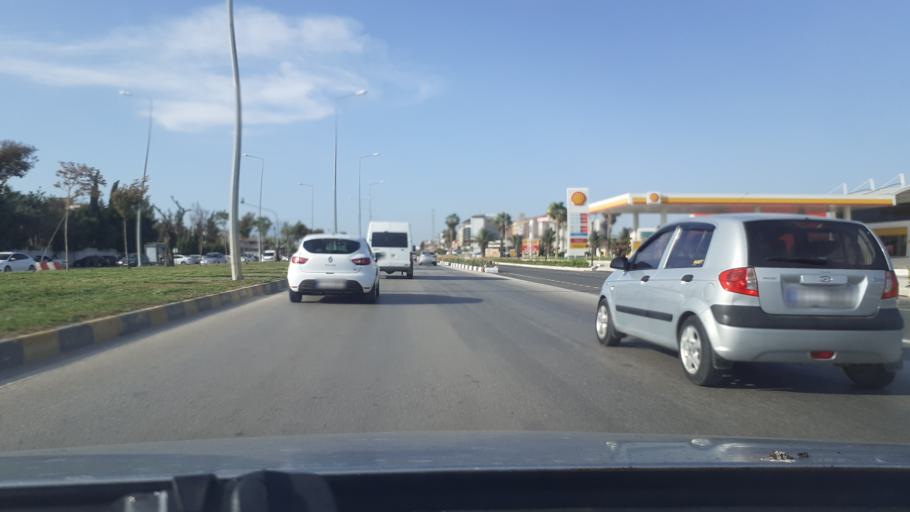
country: TR
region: Hatay
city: Kuzeytepe
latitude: 36.2454
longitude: 36.1741
